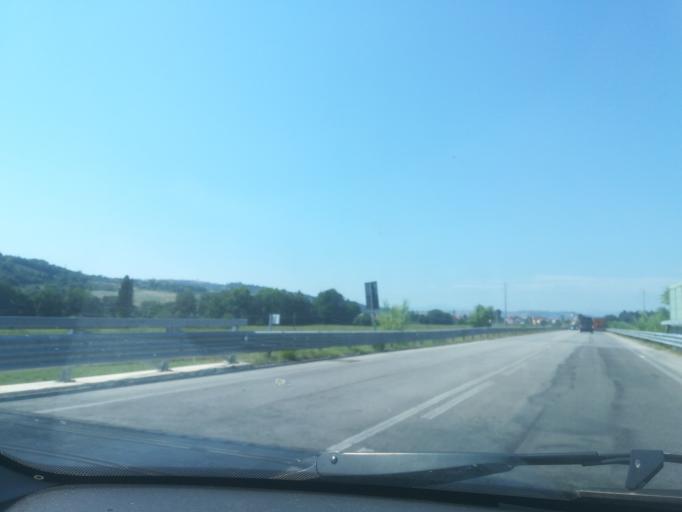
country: IT
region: The Marches
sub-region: Provincia di Macerata
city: Villa Potenza
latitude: 43.3305
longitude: 13.4346
